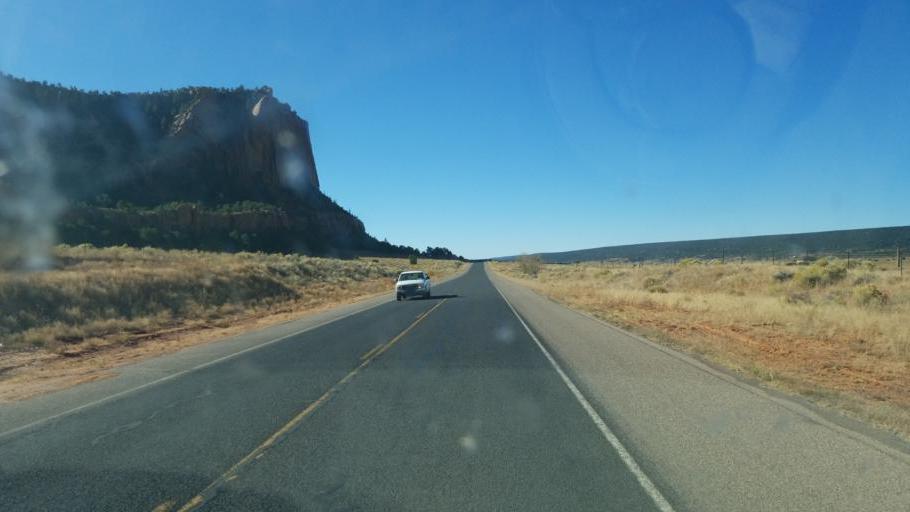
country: US
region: New Mexico
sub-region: McKinley County
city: Navajo
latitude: 35.8369
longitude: -109.0255
